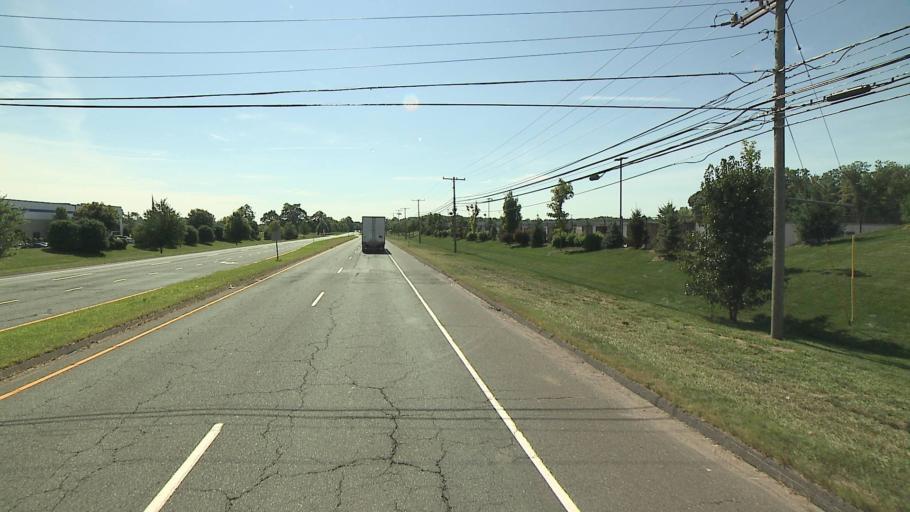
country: US
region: Connecticut
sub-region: Hartford County
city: Tariffville
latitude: 41.8708
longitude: -72.7241
